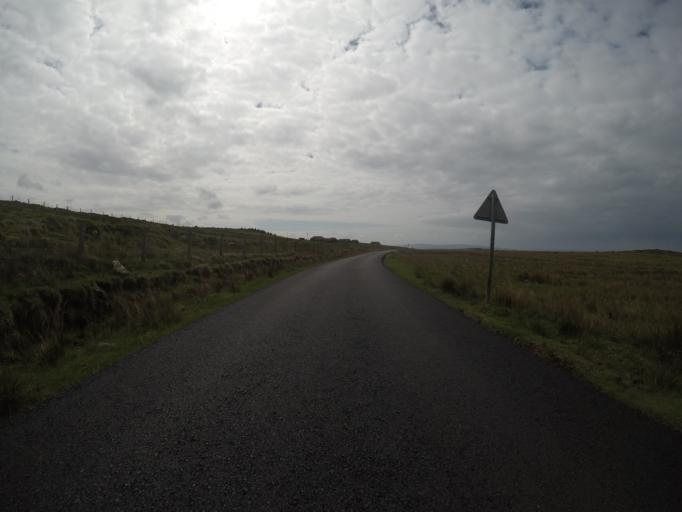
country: GB
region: Scotland
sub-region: Highland
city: Portree
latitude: 57.6622
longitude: -6.3664
